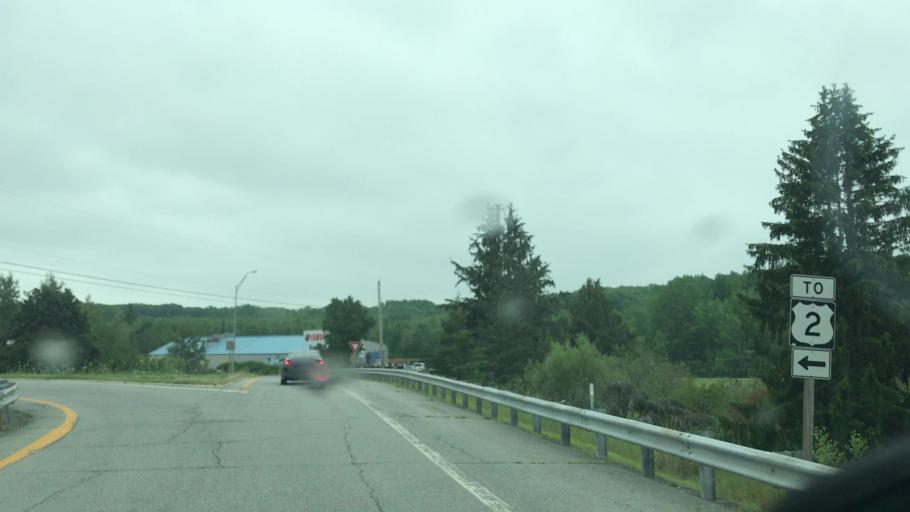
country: US
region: Maine
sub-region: Penobscot County
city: Orono
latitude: 44.9024
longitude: -68.6929
